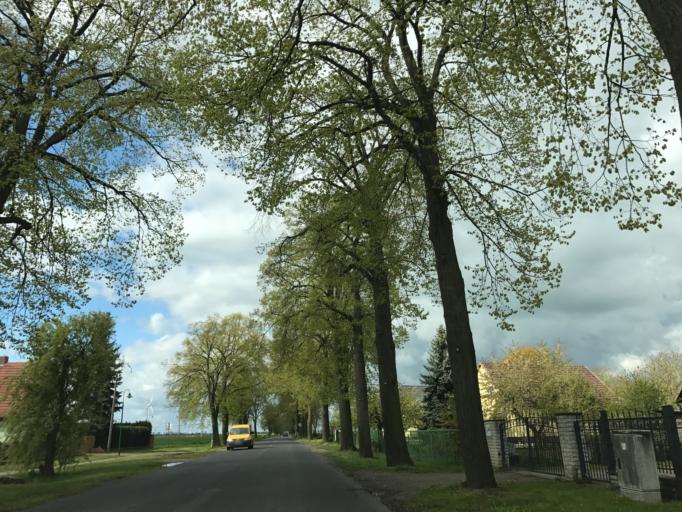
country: DE
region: Brandenburg
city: Wustermark
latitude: 52.5850
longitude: 12.9214
